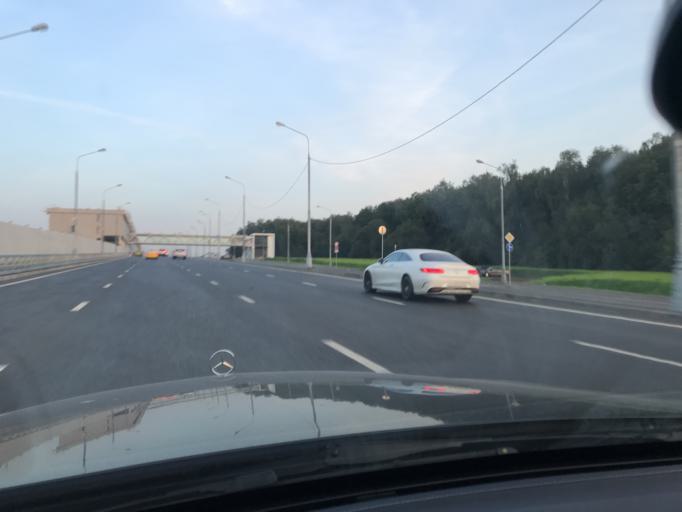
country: RU
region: Moskovskaya
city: Mosrentgen
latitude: 55.5877
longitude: 37.4294
